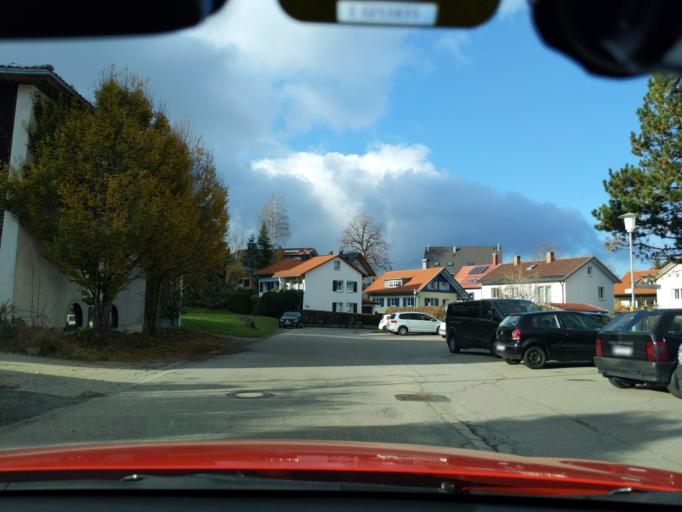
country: DE
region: Bavaria
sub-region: Swabia
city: Scheidegg
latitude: 47.5786
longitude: 9.8441
